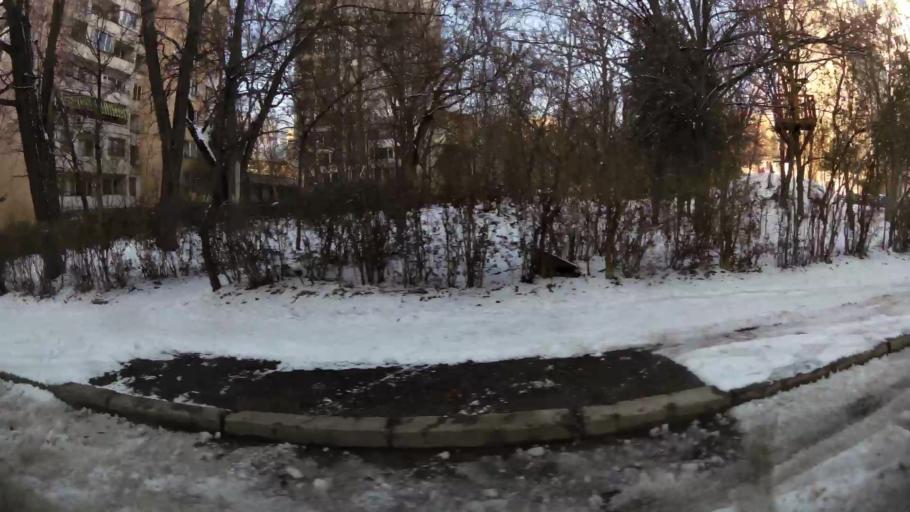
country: BG
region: Sofia-Capital
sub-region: Stolichna Obshtina
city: Sofia
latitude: 42.6677
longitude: 23.3457
